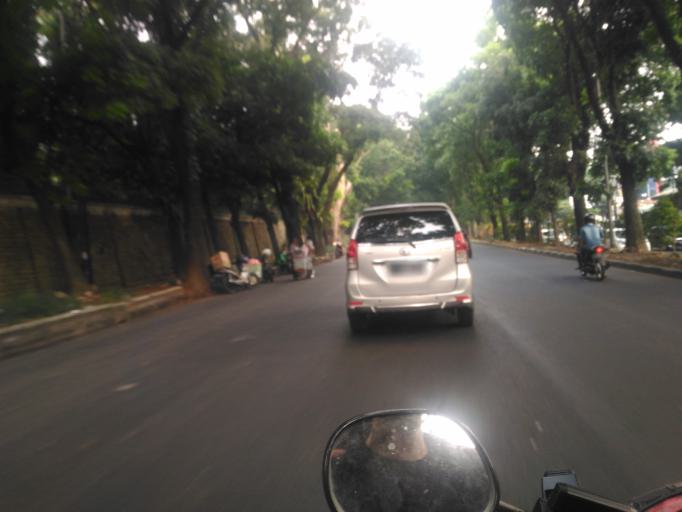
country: ID
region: West Java
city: Bogor
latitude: -6.6094
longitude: 106.8111
